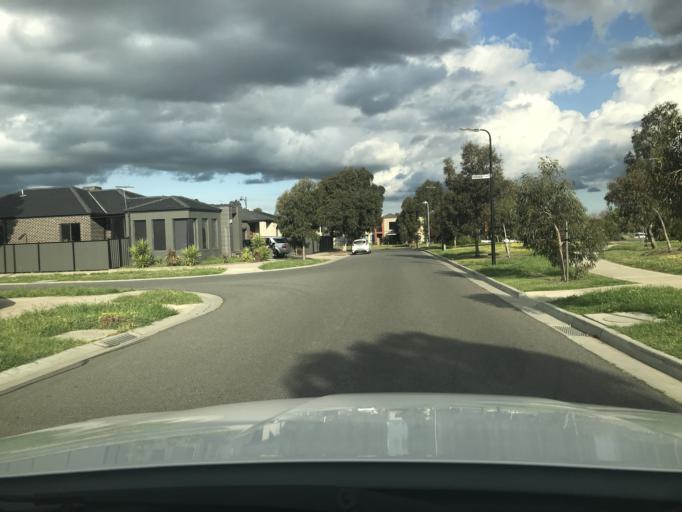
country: AU
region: Victoria
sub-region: Hume
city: Craigieburn
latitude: -37.5770
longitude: 144.9048
